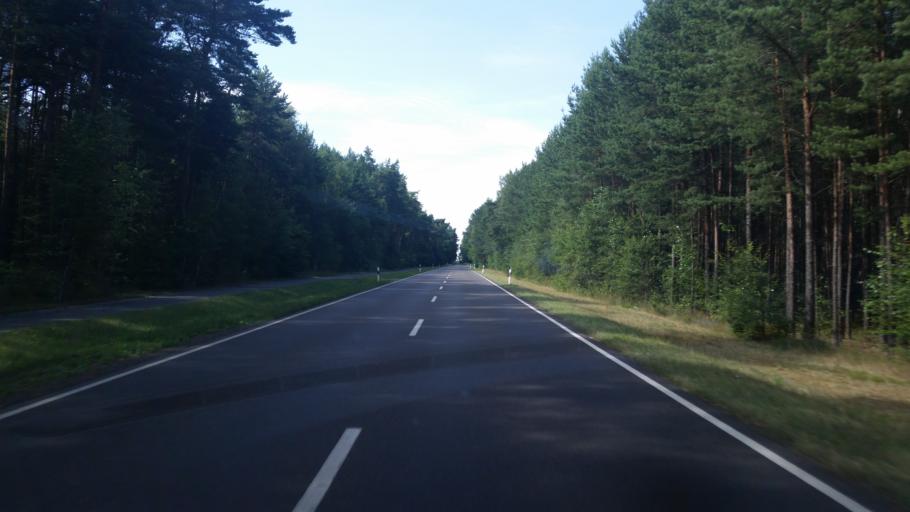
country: DE
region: Saxony
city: Bernsdorf
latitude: 51.3382
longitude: 14.0716
